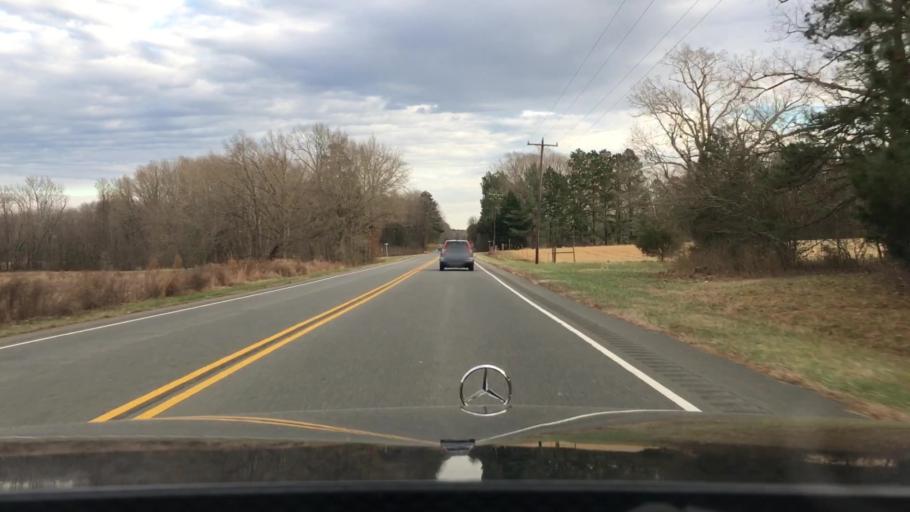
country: US
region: North Carolina
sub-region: Orange County
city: Hillsborough
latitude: 36.2106
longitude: -79.1649
